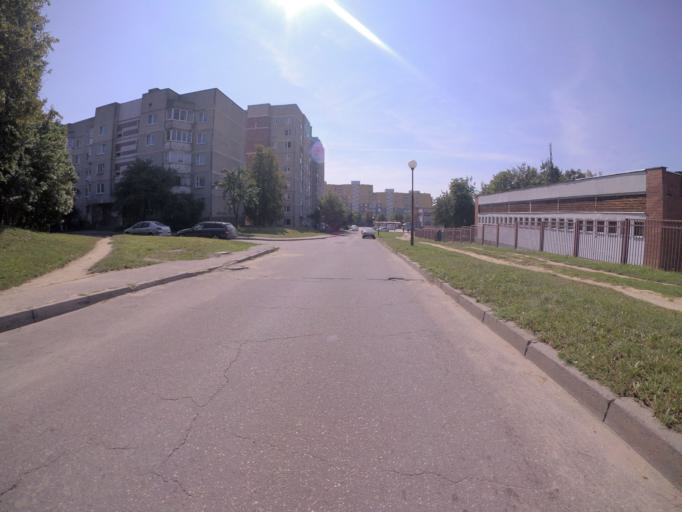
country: BY
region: Grodnenskaya
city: Hrodna
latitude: 53.7027
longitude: 23.8459
